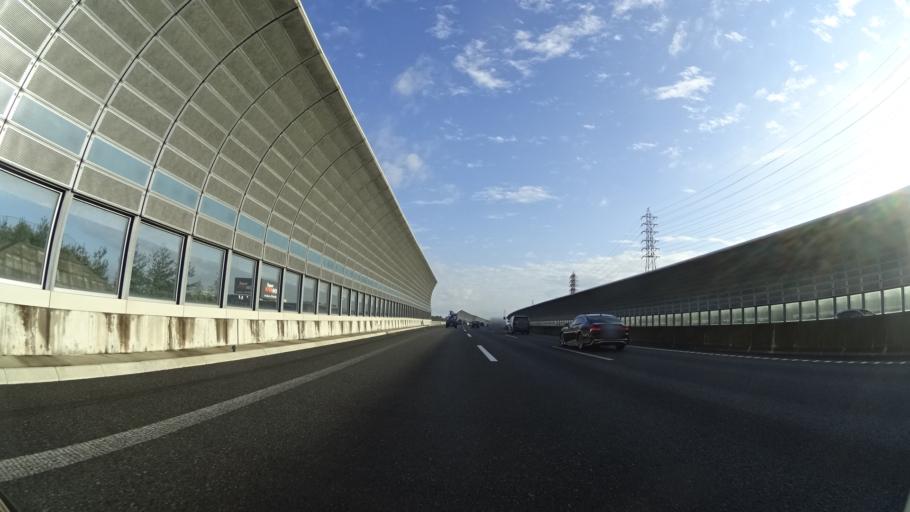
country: JP
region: Osaka
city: Neyagawa
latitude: 34.7641
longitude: 135.6516
